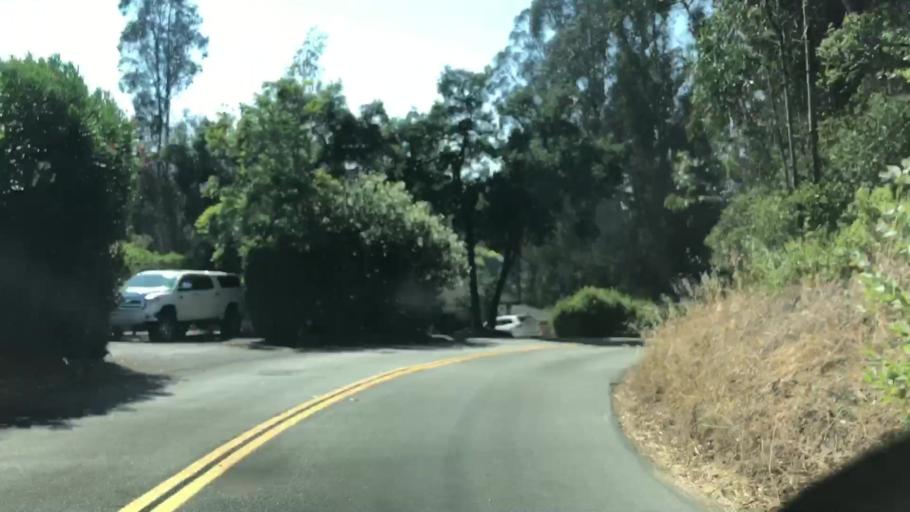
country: US
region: California
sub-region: Santa Cruz County
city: Aptos Hills-Larkin Valley
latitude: 36.9873
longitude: -121.8338
